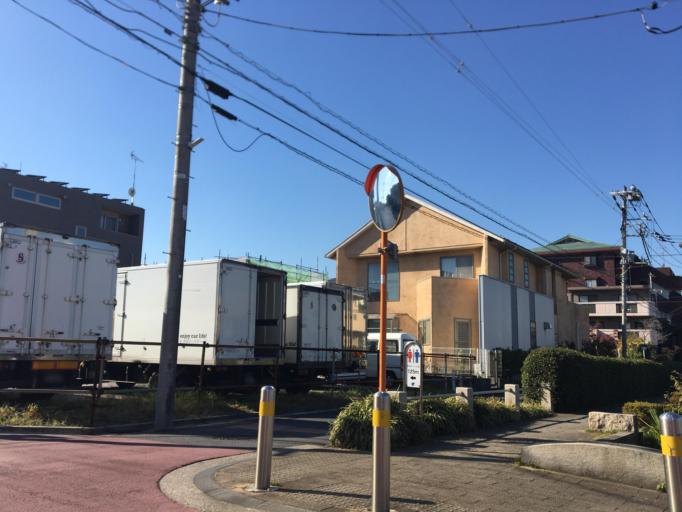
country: JP
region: Tokyo
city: Urayasu
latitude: 35.6928
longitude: 139.9053
